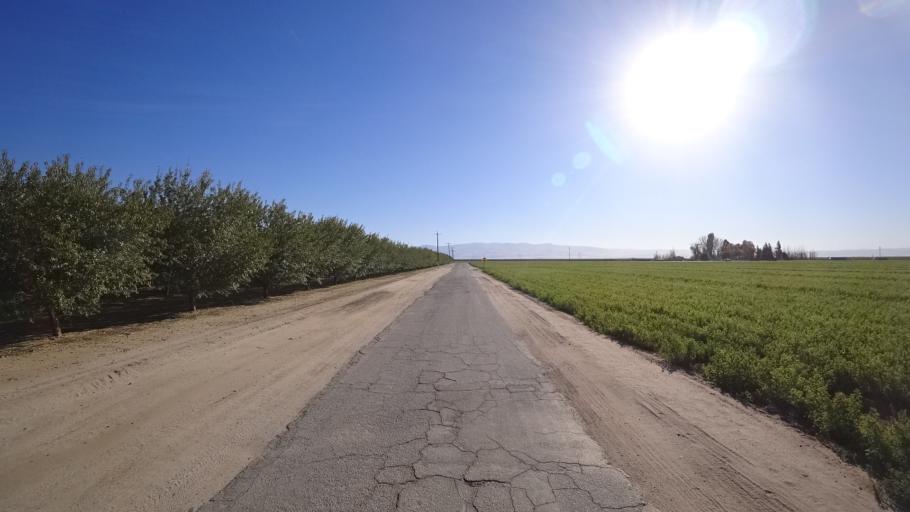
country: US
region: California
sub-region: Kern County
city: Greenacres
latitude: 35.2697
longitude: -119.1185
